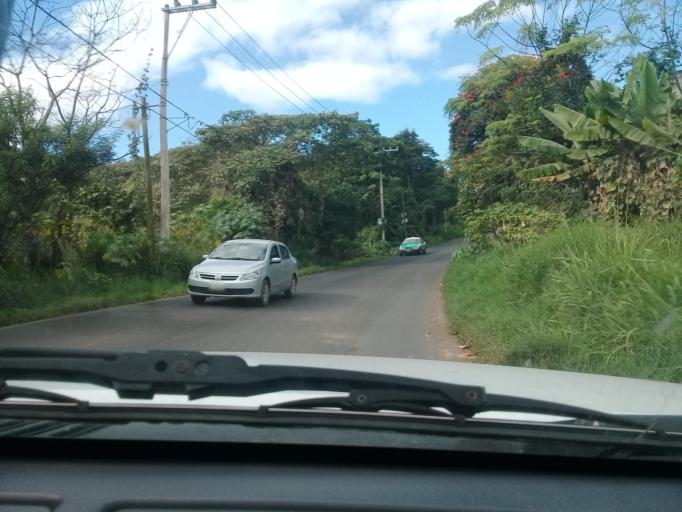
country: MX
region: Veracruz
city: El Castillo
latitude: 19.5468
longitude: -96.8833
